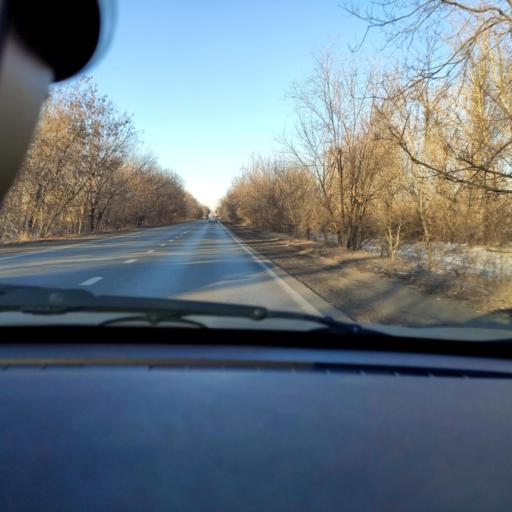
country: RU
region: Samara
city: Tol'yatti
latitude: 53.5468
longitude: 49.3936
